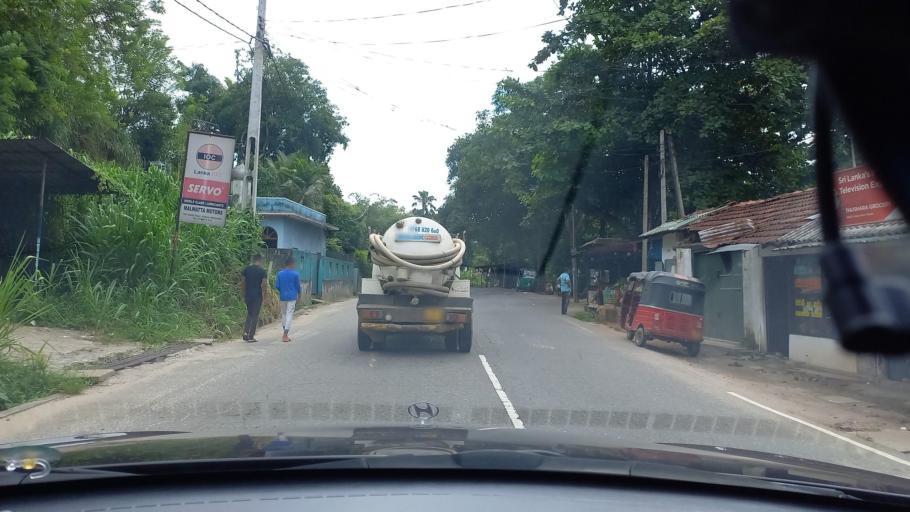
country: LK
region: Central
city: Kadugannawa
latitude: 7.2476
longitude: 80.4681
